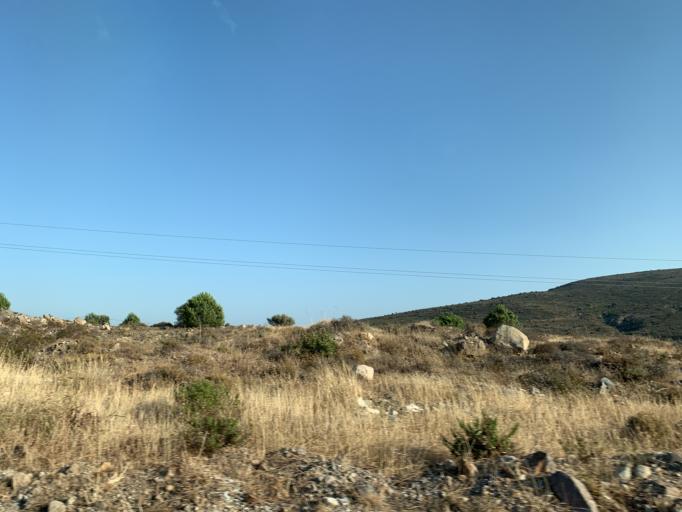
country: TR
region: Izmir
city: Alacati
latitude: 38.2761
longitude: 26.4124
